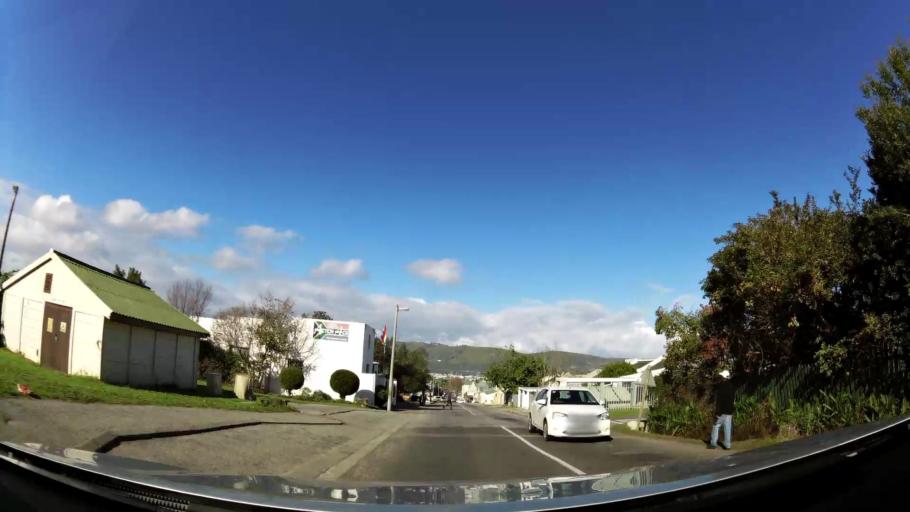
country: ZA
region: Western Cape
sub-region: Eden District Municipality
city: Knysna
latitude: -34.0333
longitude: 23.0469
